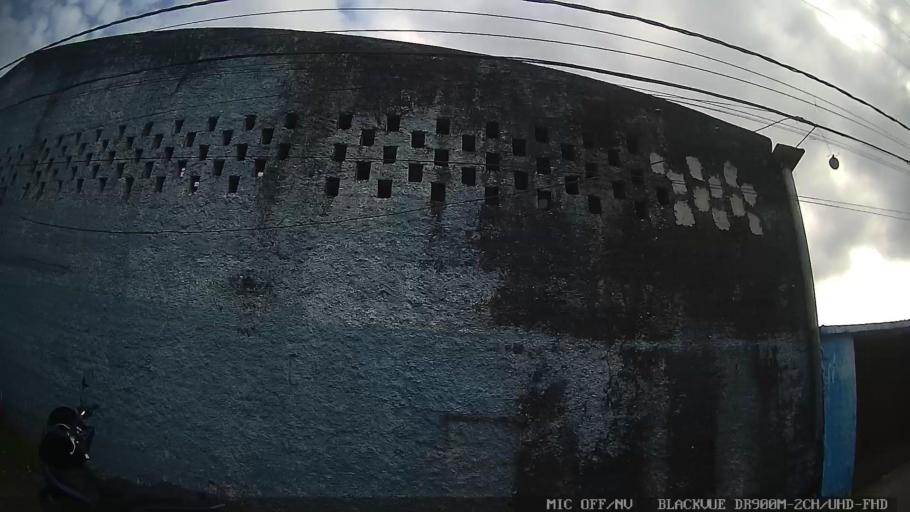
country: BR
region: Sao Paulo
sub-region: Guaruja
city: Guaruja
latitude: -23.9595
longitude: -46.2770
